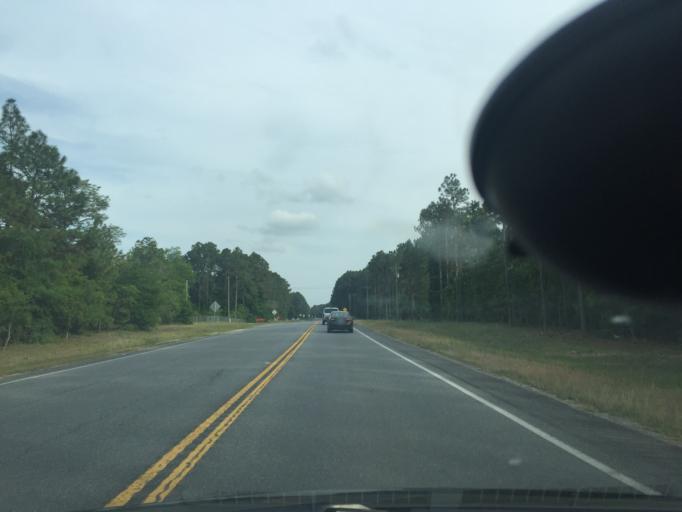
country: US
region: Georgia
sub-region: Chatham County
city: Bloomingdale
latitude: 32.0517
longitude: -81.3419
